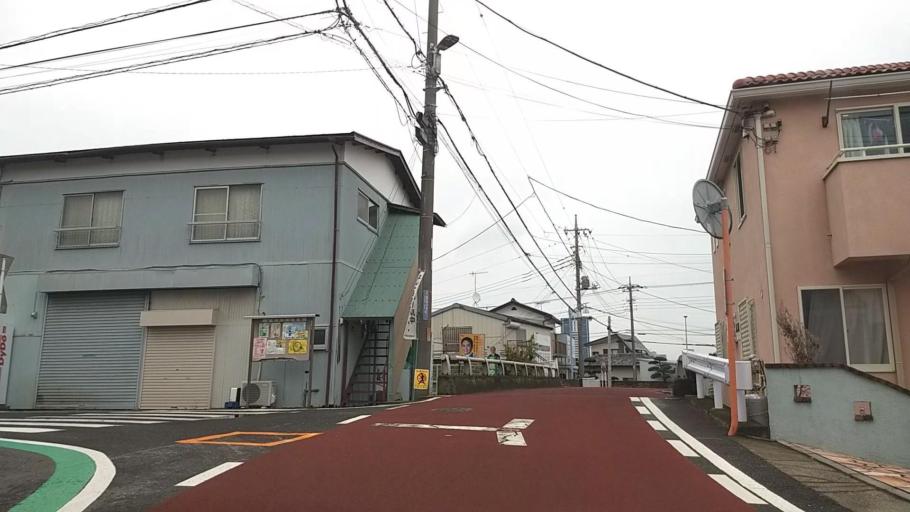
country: JP
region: Kanagawa
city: Atsugi
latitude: 35.4194
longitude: 139.3478
